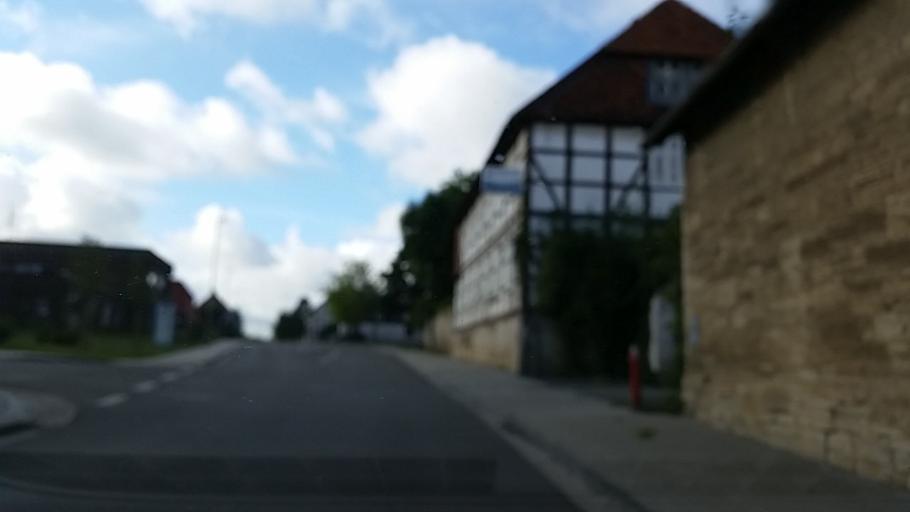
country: DE
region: Lower Saxony
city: Cremlingen
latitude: 52.2468
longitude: 10.6541
